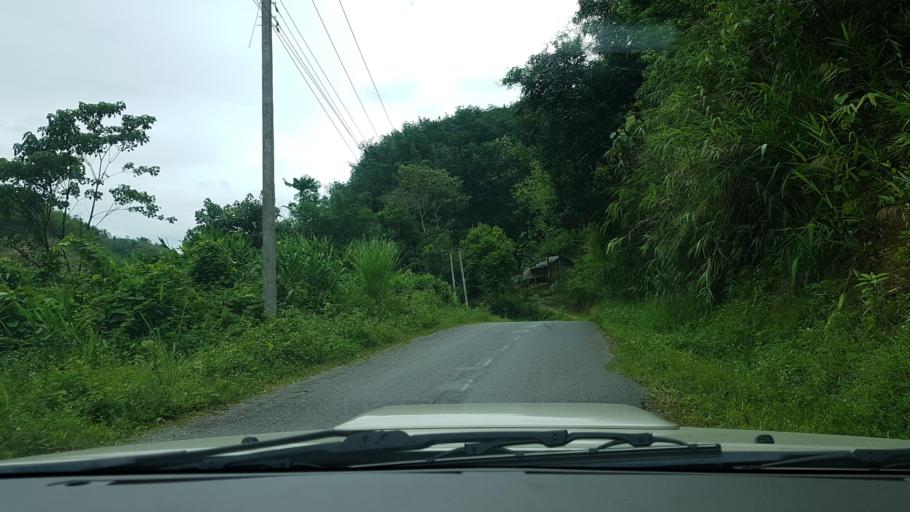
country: LA
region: Phongsali
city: Khoa
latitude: 21.0616
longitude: 102.3840
